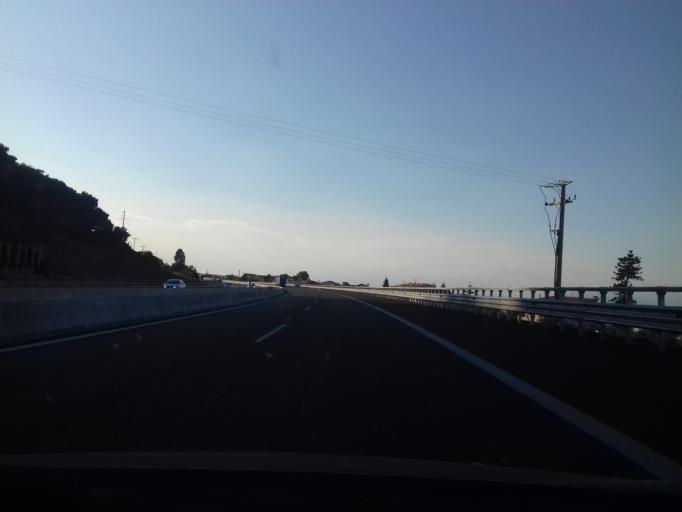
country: GR
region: Peloponnese
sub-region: Nomos Korinthias
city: Kato Dhiminio
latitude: 38.0392
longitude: 22.7090
